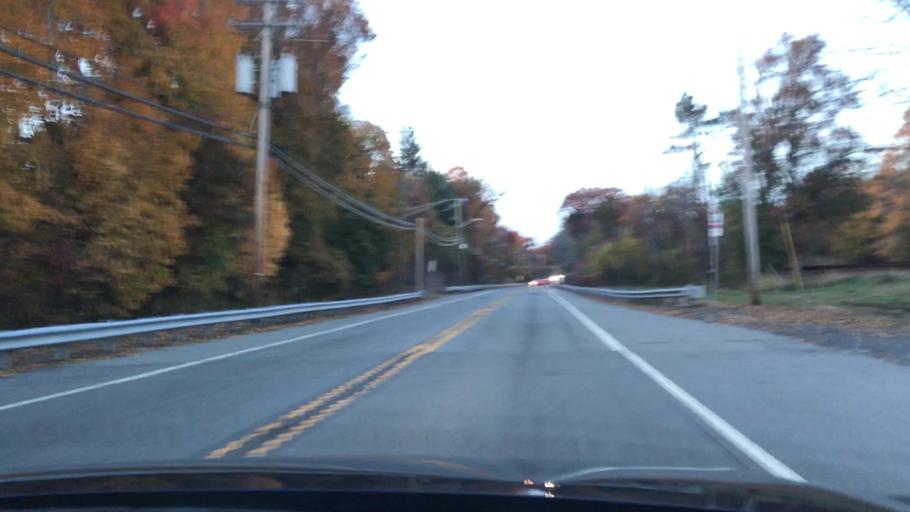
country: US
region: New Jersey
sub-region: Bergen County
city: Alpine
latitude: 40.9480
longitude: -73.9231
